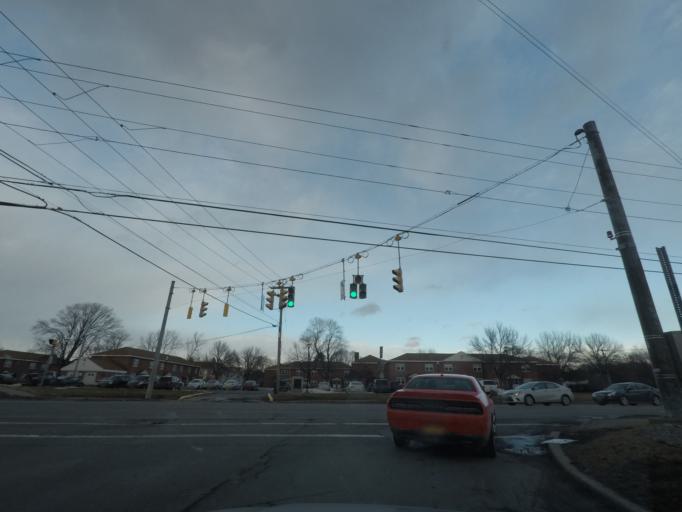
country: US
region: New York
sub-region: Oneida County
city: Utica
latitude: 43.1145
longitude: -75.2056
